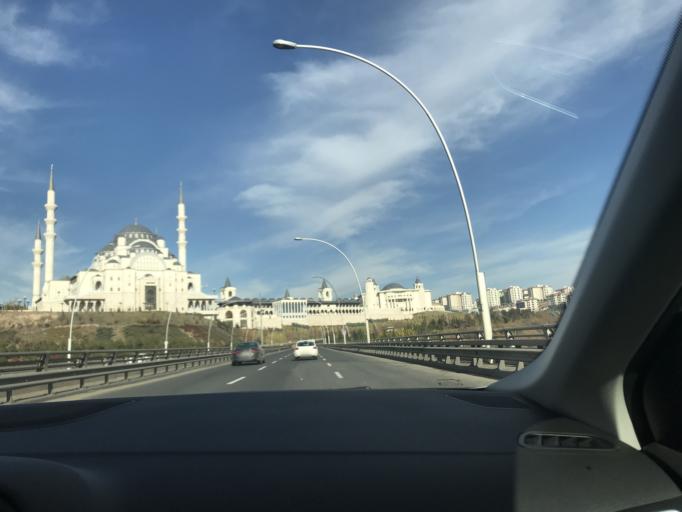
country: TR
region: Ankara
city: Mamak
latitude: 40.0046
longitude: 32.8921
